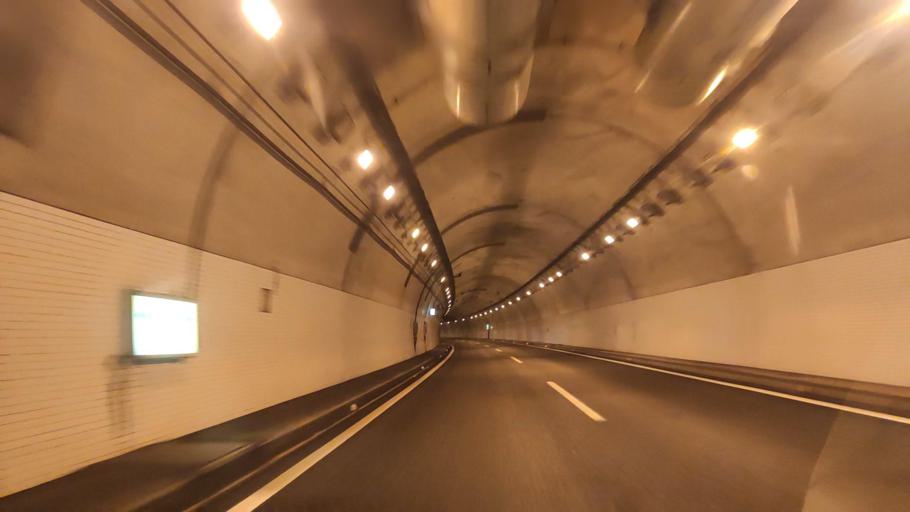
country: JP
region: Niigata
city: Itoigawa
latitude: 37.0070
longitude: 137.7435
